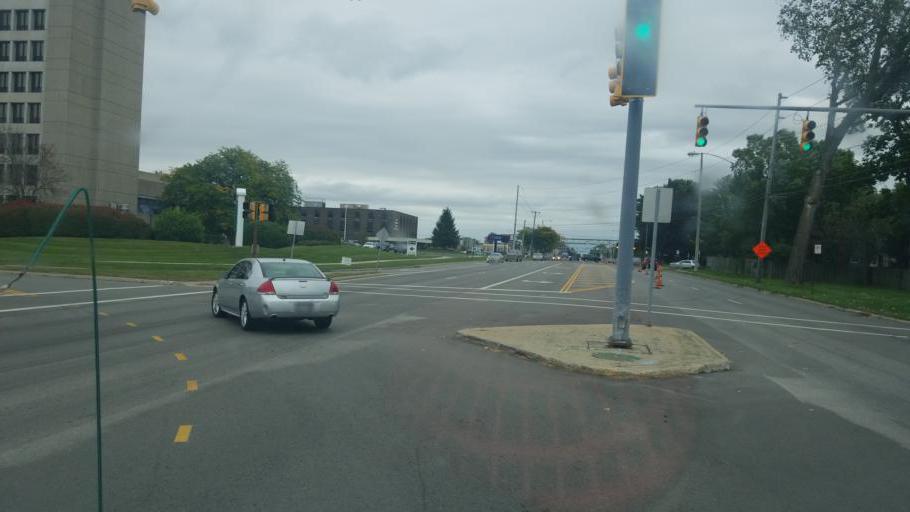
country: US
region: Ohio
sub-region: Lucas County
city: Ottawa Hills
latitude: 41.6773
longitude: -83.6295
